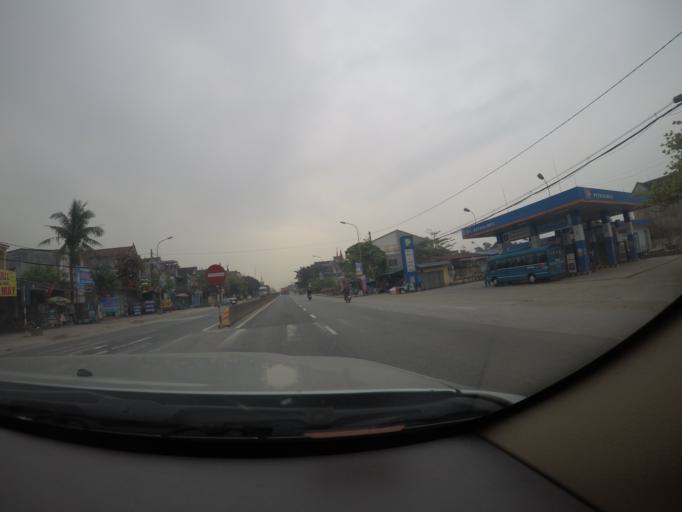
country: VN
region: Ha Tinh
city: Cam Xuyen
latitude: 18.2531
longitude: 105.9963
